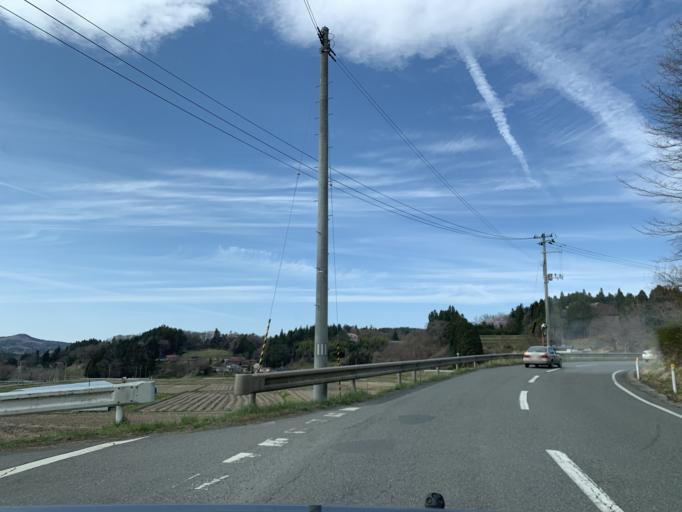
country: JP
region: Iwate
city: Ichinoseki
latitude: 38.8447
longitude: 141.3418
